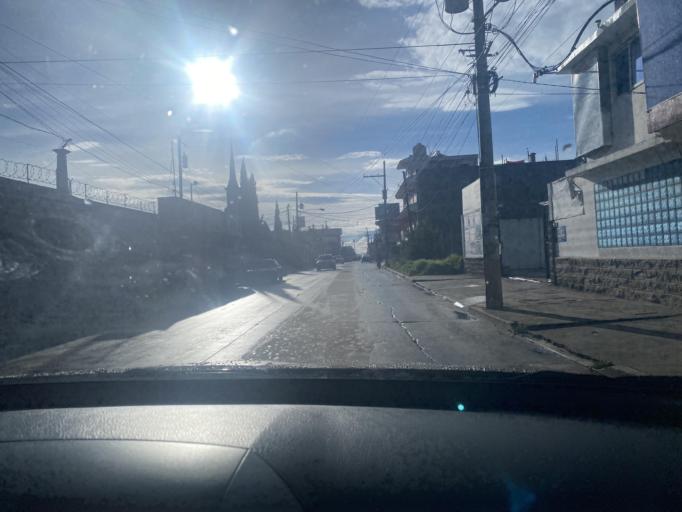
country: GT
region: Quetzaltenango
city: Olintepeque
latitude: 14.8660
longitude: -91.5175
